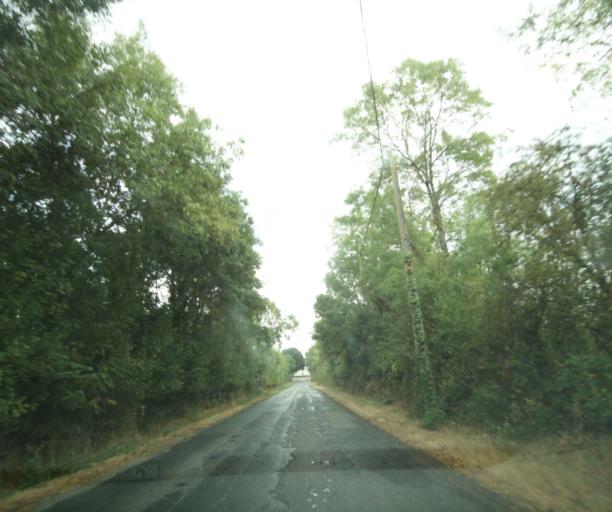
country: FR
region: Poitou-Charentes
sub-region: Departement de la Charente-Maritime
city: Tonnay-Charente
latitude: 45.9422
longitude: -0.8771
